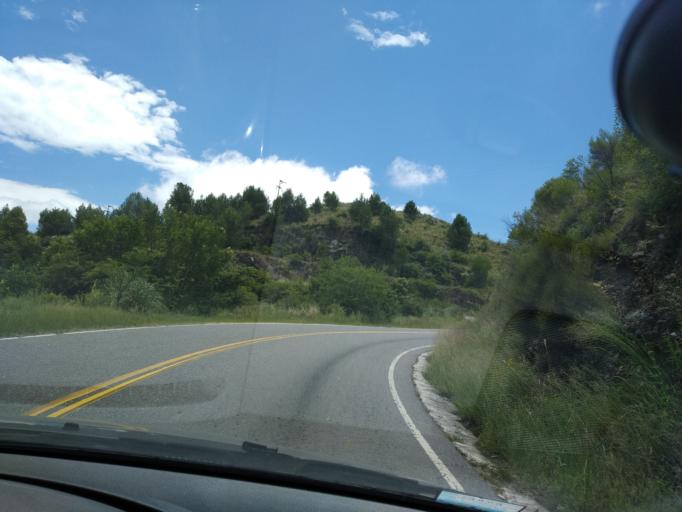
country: AR
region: Cordoba
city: Cuesta Blanca
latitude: -31.6021
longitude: -64.5441
